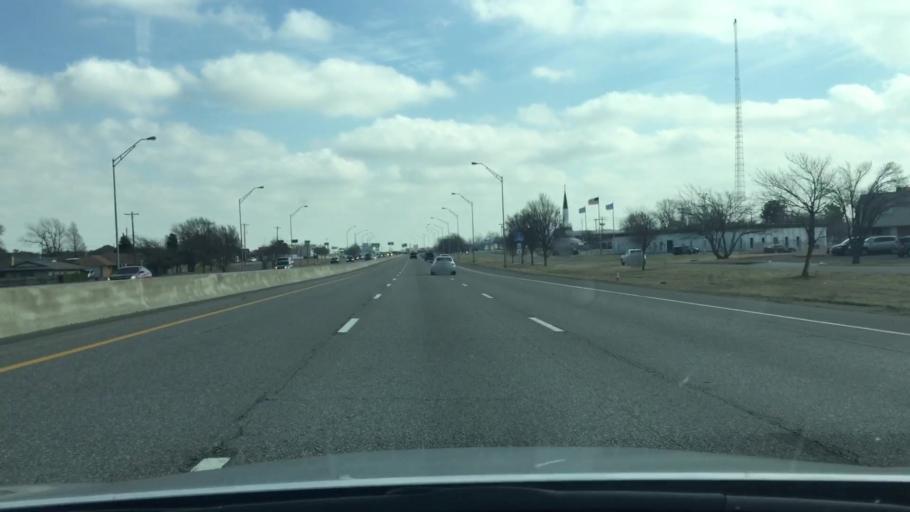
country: US
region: Oklahoma
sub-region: Oklahoma County
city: Oklahoma City
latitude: 35.3928
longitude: -97.5602
